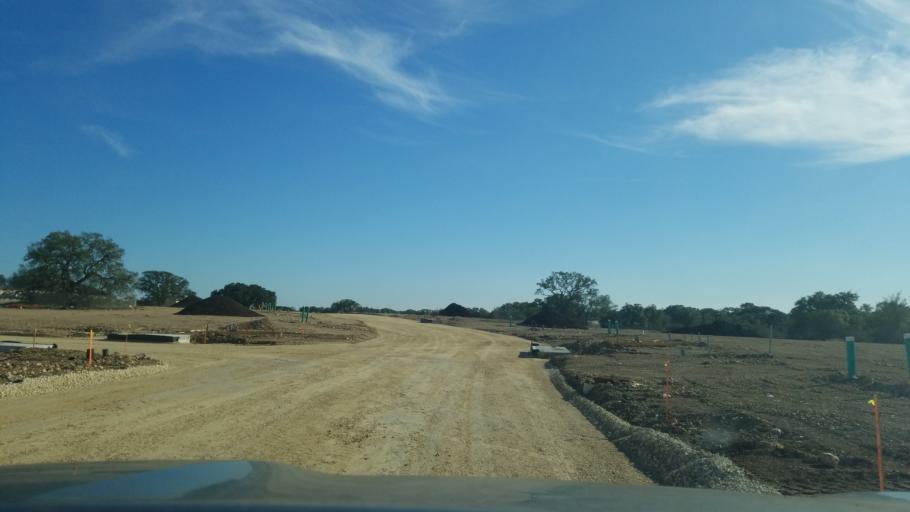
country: US
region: Texas
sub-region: Comal County
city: Canyon Lake
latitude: 29.7886
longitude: -98.2892
